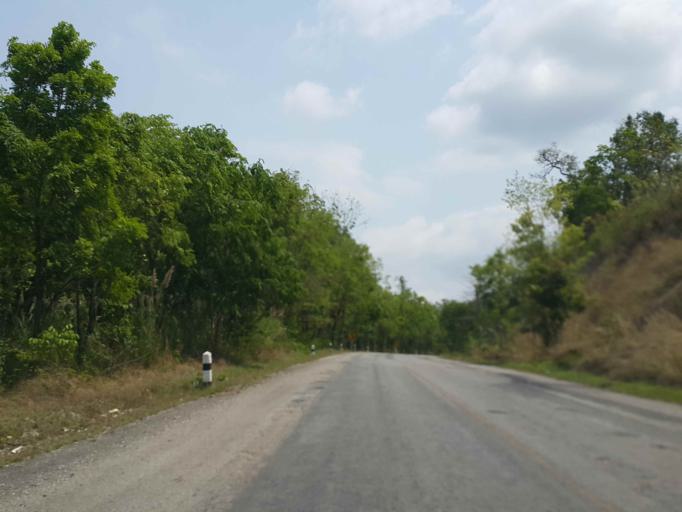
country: TH
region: Lampang
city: Thoen
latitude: 17.6296
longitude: 99.3117
